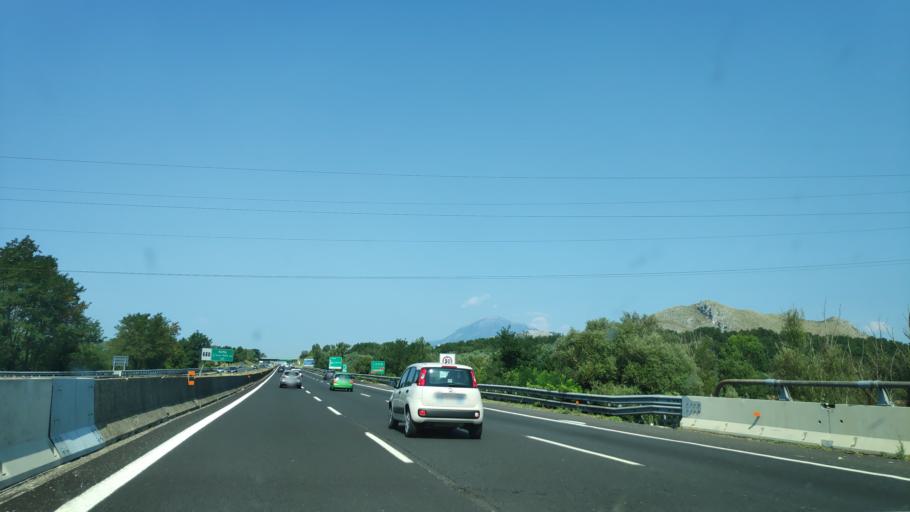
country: IT
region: Campania
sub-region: Provincia di Caserta
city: Bivio Mortola
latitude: 41.4282
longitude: 13.9097
